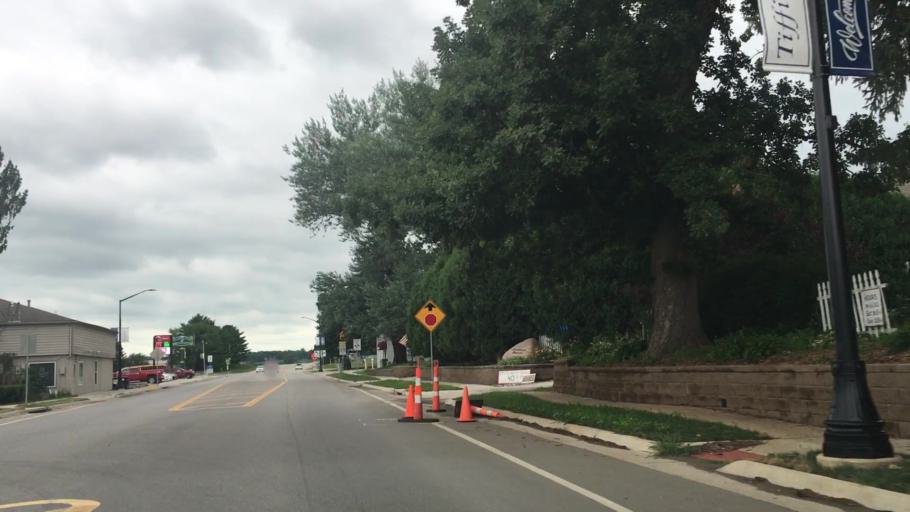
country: US
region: Iowa
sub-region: Johnson County
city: Tiffin
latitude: 41.7071
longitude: -91.6644
